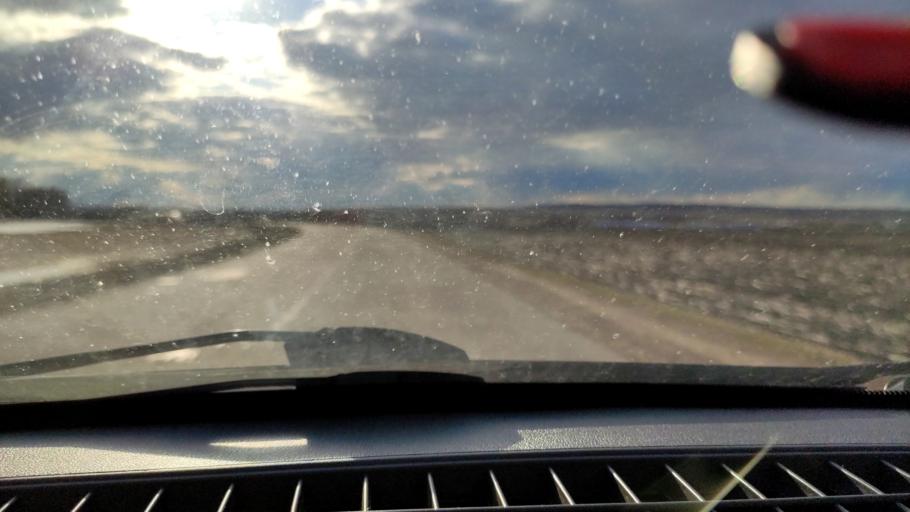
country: RU
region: Bashkortostan
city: Karmaskaly
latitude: 54.3488
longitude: 56.0617
